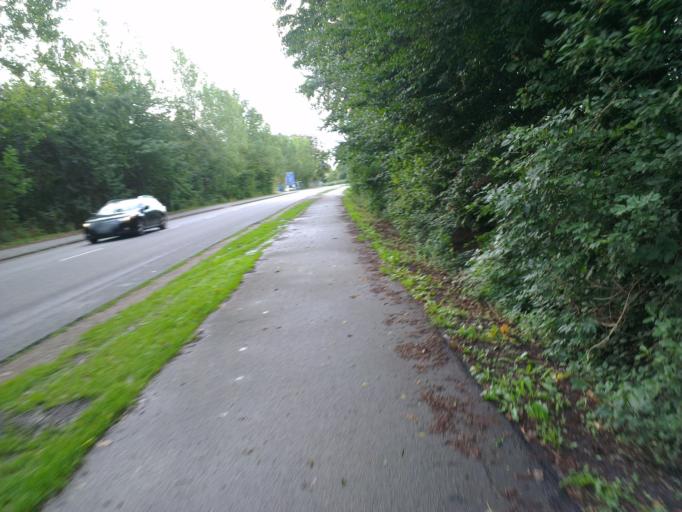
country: DK
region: Capital Region
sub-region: Frederikssund Kommune
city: Frederikssund
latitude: 55.8222
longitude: 12.0922
